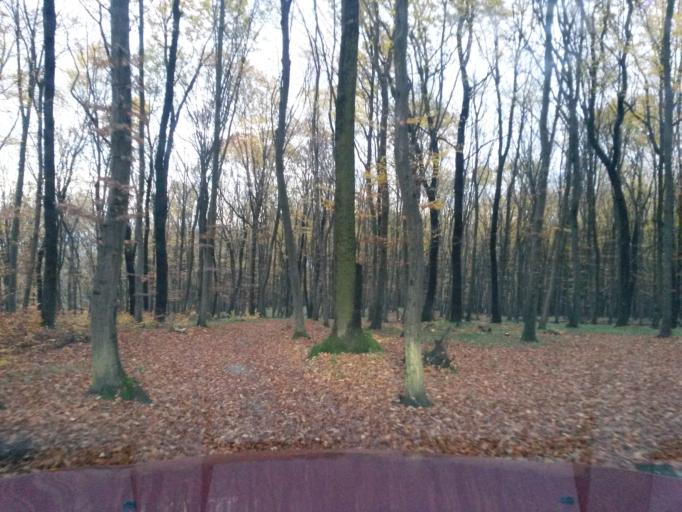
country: SK
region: Kosicky
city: Kosice
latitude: 48.7955
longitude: 21.2832
